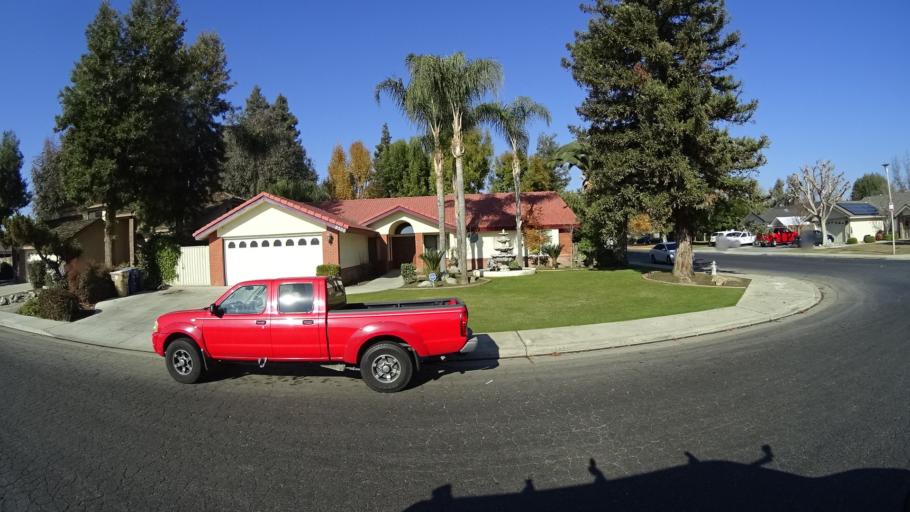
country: US
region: California
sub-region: Kern County
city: Greenacres
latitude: 35.3210
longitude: -119.1074
